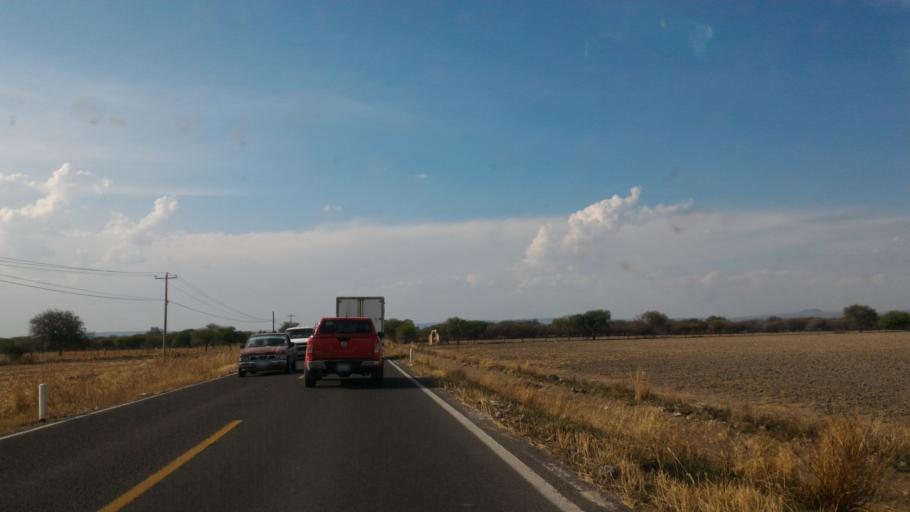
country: MX
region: Guanajuato
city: Ciudad Manuel Doblado
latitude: 20.7662
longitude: -101.9707
